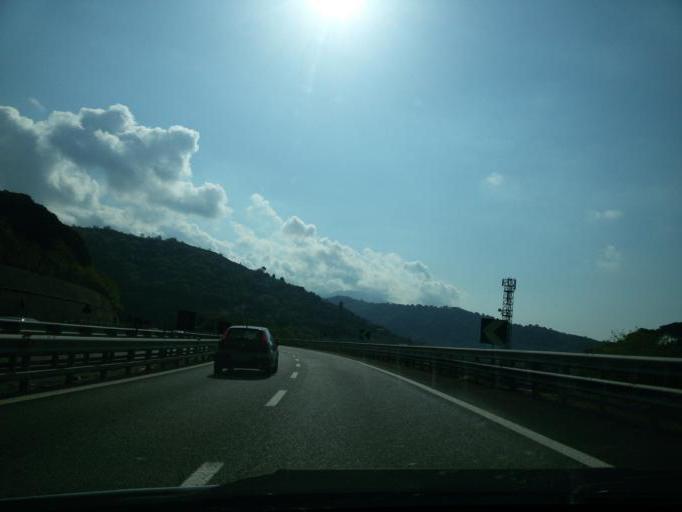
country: IT
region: Liguria
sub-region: Provincia di Genova
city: Genoa
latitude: 44.4372
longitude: 8.9411
